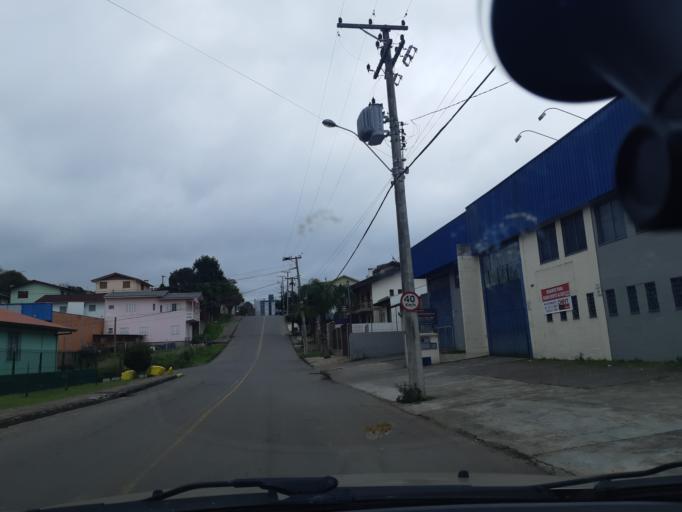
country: BR
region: Rio Grande do Sul
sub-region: Caxias Do Sul
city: Caxias do Sul
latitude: -29.1589
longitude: -51.2067
